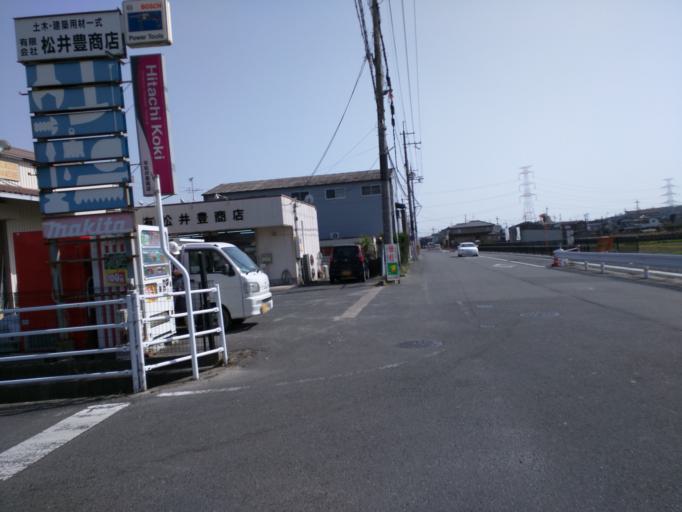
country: JP
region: Kyoto
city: Tanabe
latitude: 34.7617
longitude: 135.7973
